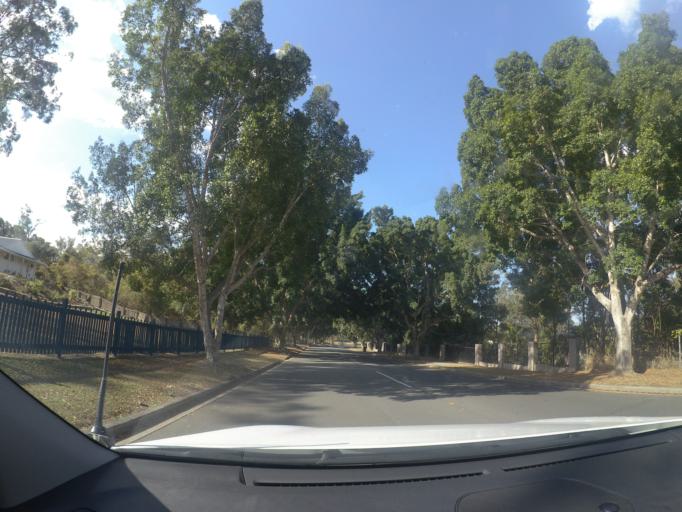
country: AU
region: Queensland
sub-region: Logan
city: Woodridge
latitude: -27.6523
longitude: 153.0634
